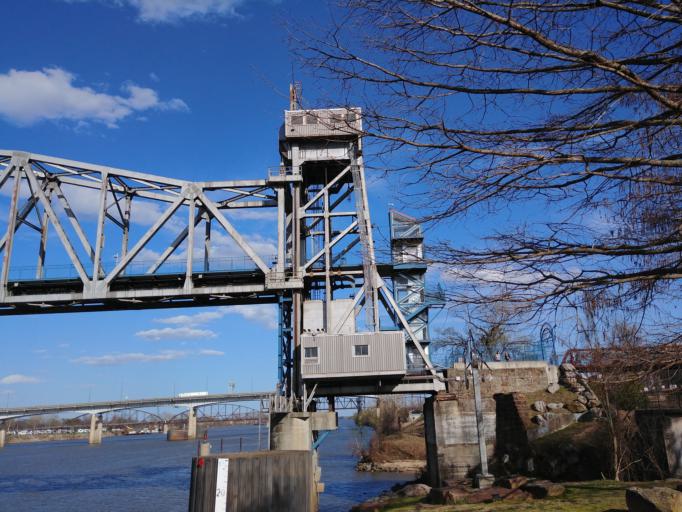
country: US
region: Arkansas
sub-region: Pulaski County
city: North Little Rock
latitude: 34.7494
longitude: -92.2674
